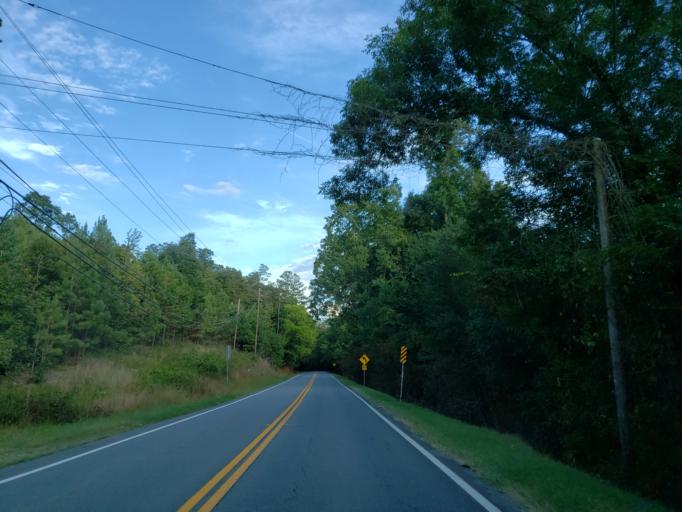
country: US
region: Georgia
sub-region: Bartow County
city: Euharlee
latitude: 34.2422
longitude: -84.9085
